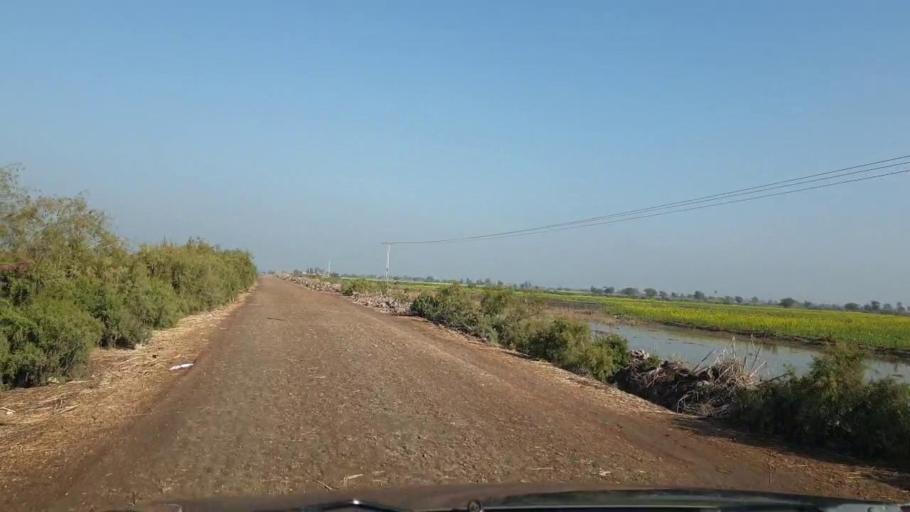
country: PK
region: Sindh
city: Sinjhoro
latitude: 26.0355
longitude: 68.7889
